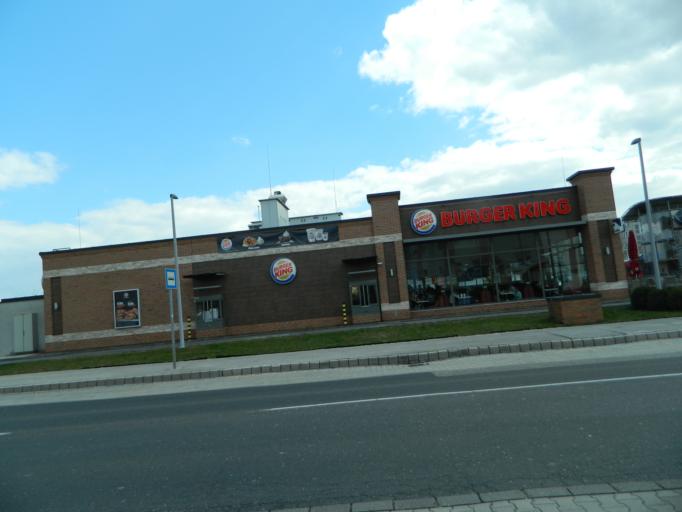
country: HU
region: Fejer
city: Szekesfehervar
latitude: 47.1827
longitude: 18.4071
